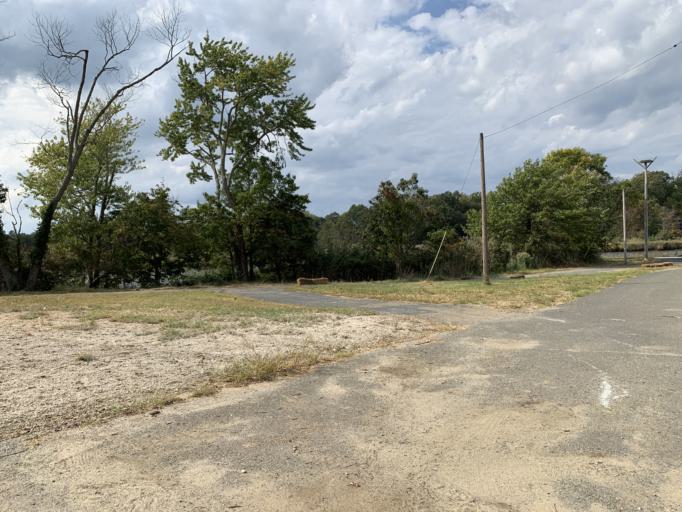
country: US
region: New Jersey
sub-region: Monmouth County
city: Little Silver
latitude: 40.3193
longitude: -74.0404
